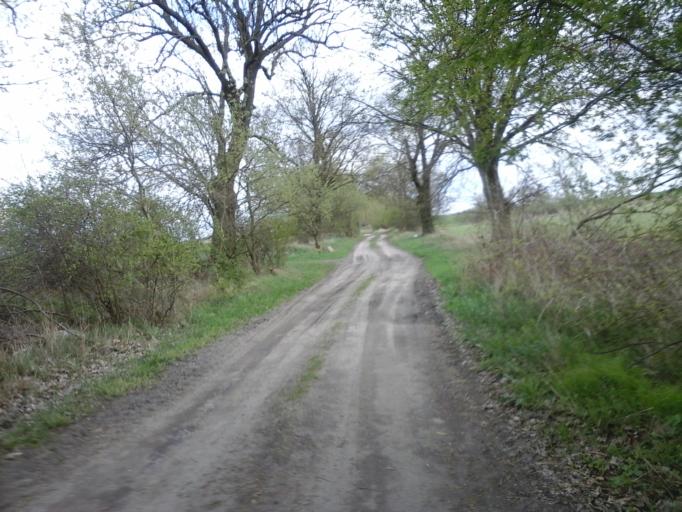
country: PL
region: West Pomeranian Voivodeship
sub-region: Powiat choszczenski
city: Krzecin
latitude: 53.1132
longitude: 15.5027
